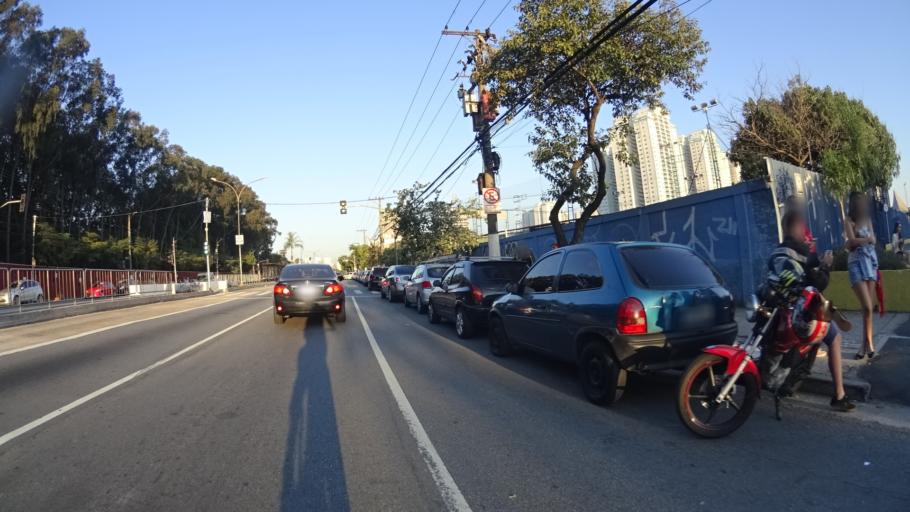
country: BR
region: Sao Paulo
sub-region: Sao Paulo
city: Sao Paulo
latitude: -23.5164
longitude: -46.6857
